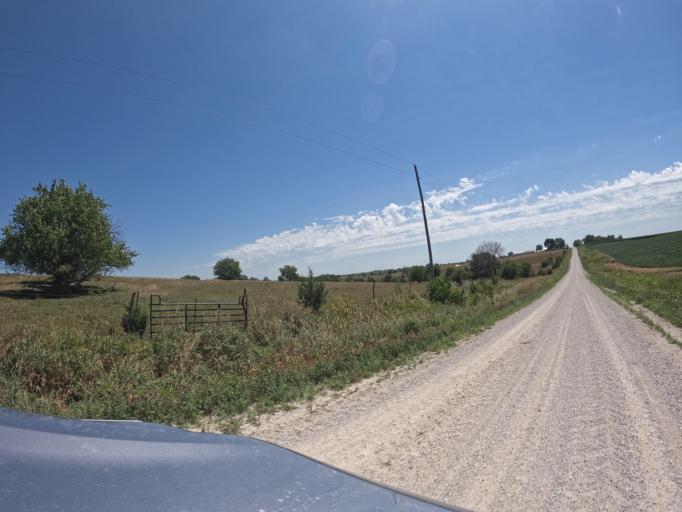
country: US
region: Iowa
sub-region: Keokuk County
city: Sigourney
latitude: 41.4197
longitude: -92.3163
